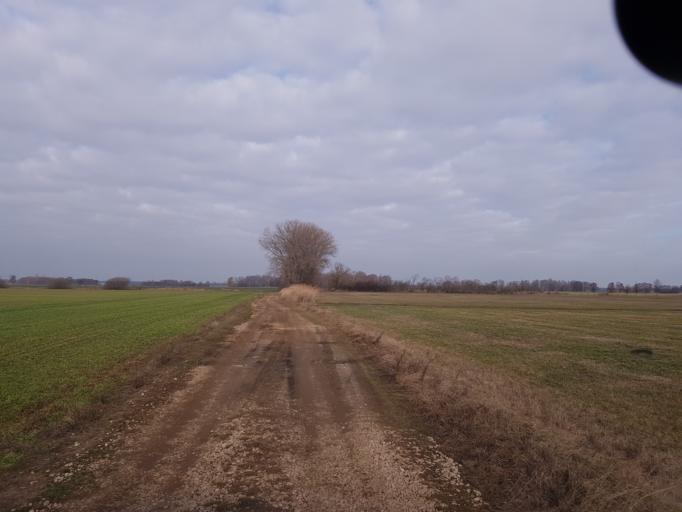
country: DE
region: Brandenburg
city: Doberlug-Kirchhain
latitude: 51.6649
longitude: 13.5648
